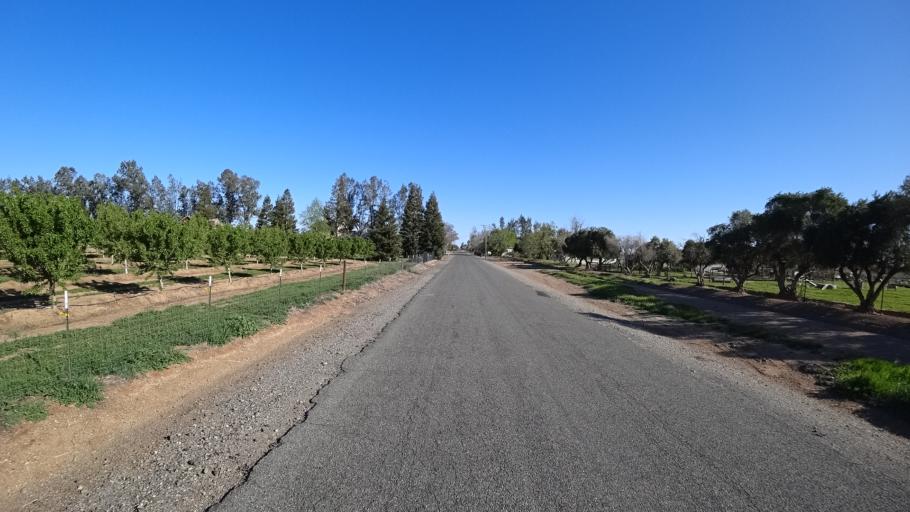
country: US
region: California
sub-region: Glenn County
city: Orland
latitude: 39.7359
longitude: -122.2391
